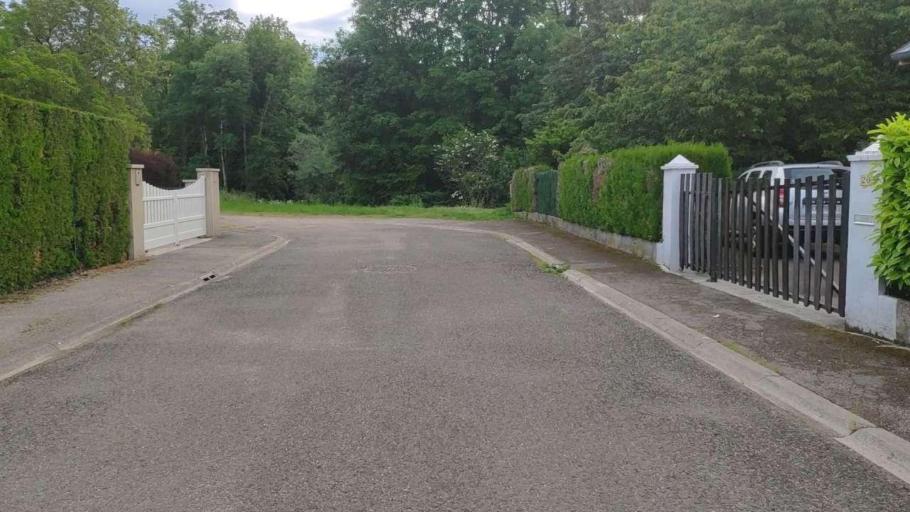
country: FR
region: Franche-Comte
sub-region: Departement du Jura
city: Perrigny
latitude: 46.7594
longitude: 5.6096
